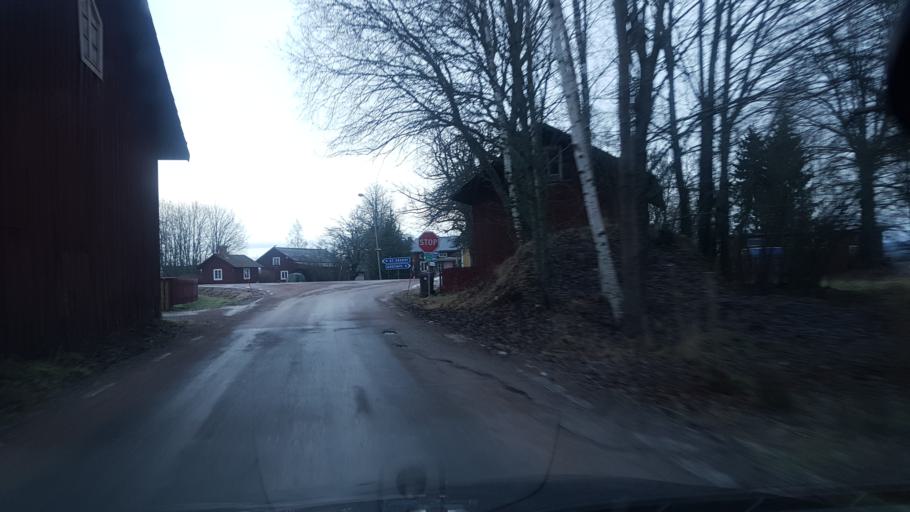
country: SE
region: Dalarna
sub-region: Saters Kommun
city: Saeter
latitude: 60.4234
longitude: 15.6558
